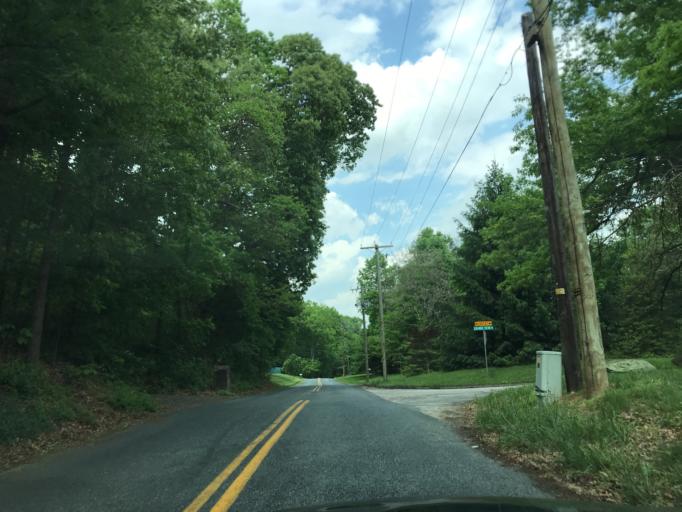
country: US
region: Pennsylvania
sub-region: York County
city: Susquehanna Trails
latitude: 39.6902
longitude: -76.3529
